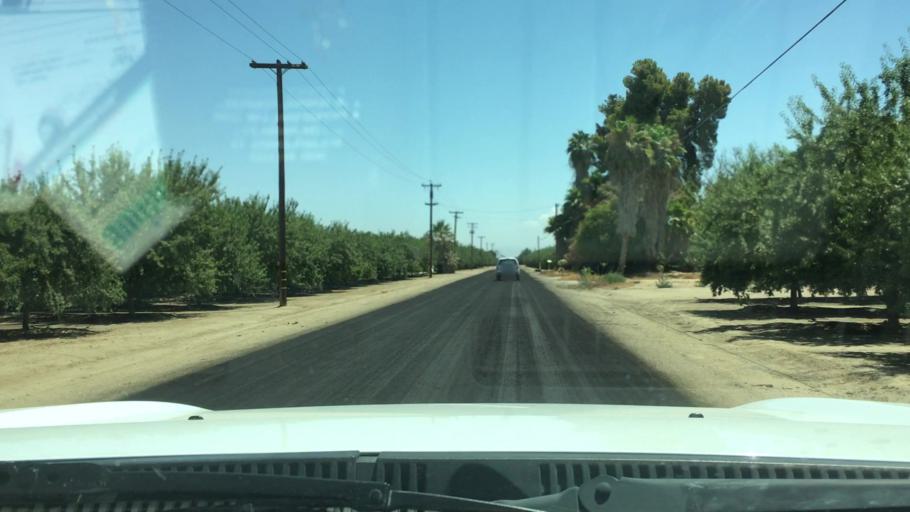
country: US
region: California
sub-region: Kern County
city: Shafter
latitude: 35.5290
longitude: -119.3284
